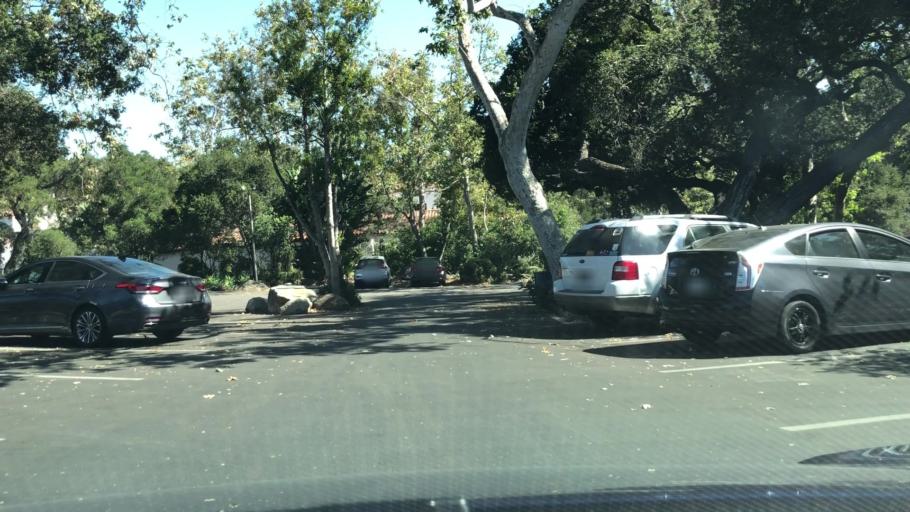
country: US
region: California
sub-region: Santa Barbara County
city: Mission Canyon
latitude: 34.4416
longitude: -119.7156
